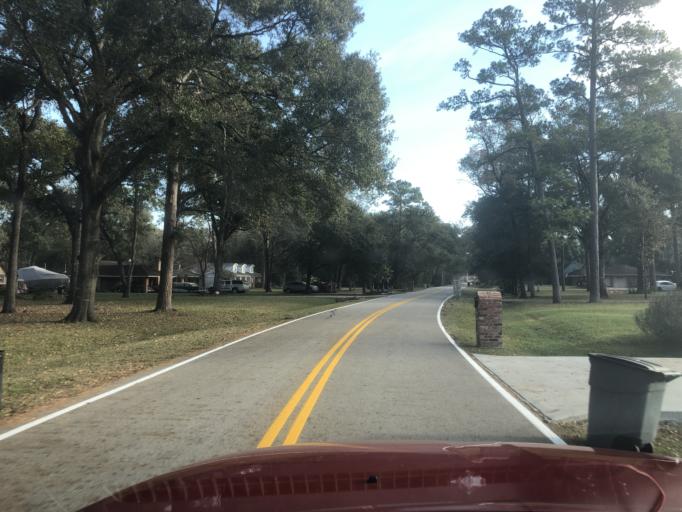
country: US
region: Texas
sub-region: Harris County
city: Spring
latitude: 30.0170
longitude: -95.4761
